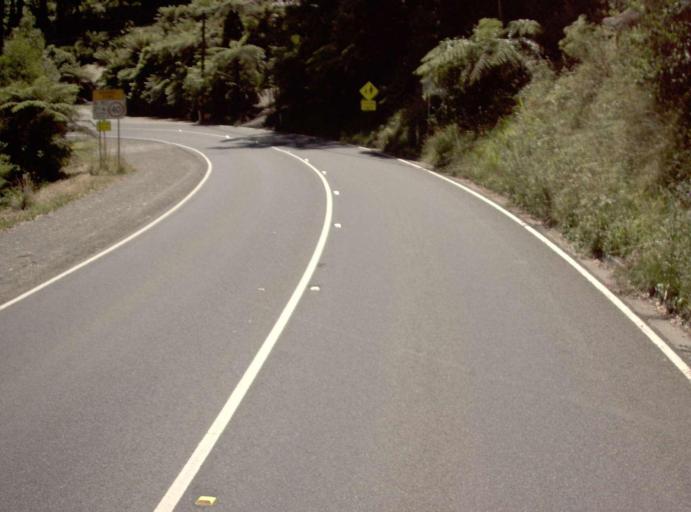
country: AU
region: Victoria
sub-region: Yarra Ranges
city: Olinda
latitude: -37.8614
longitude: 145.3566
